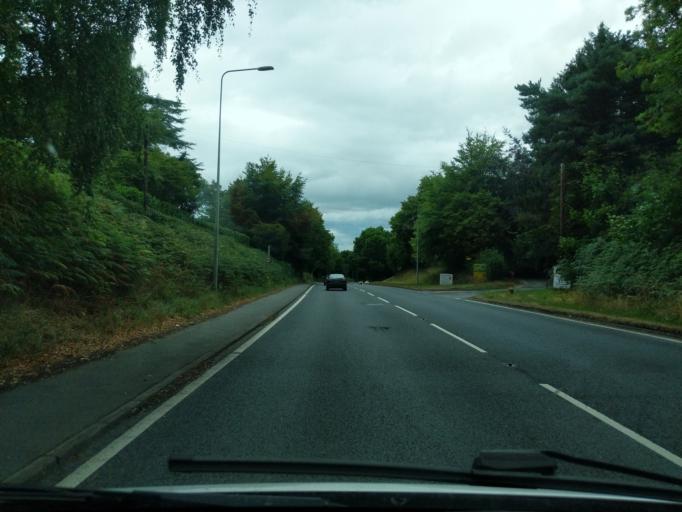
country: GB
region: England
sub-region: Cheshire West and Chester
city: Cuddington
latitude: 53.2438
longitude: -2.5993
